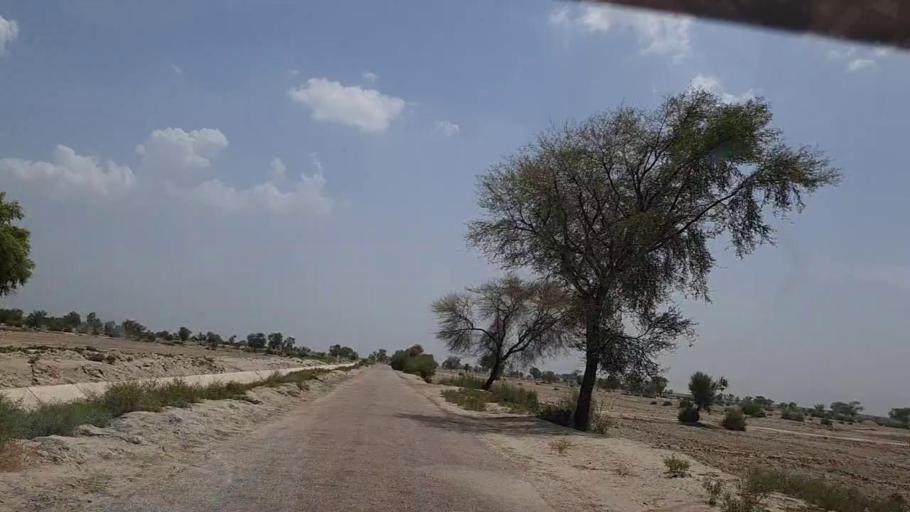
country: PK
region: Sindh
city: Bhan
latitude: 26.5354
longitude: 67.6328
